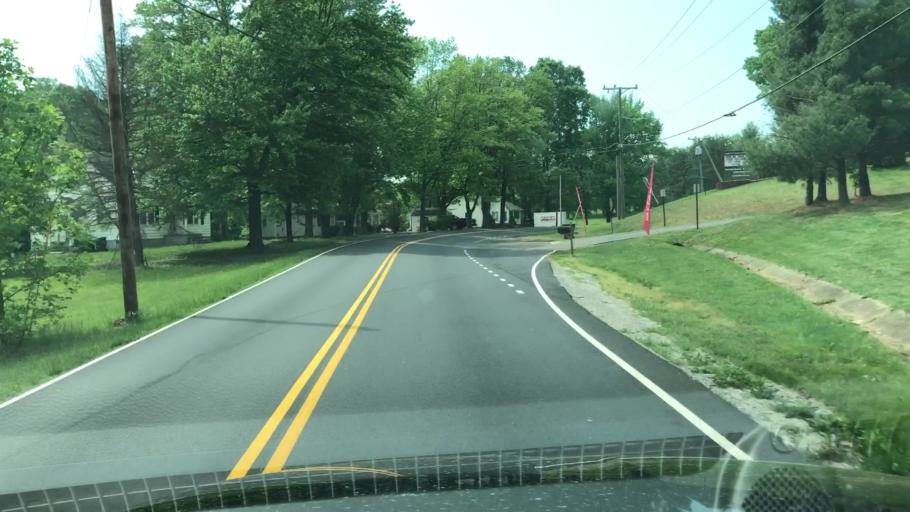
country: US
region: Virginia
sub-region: Stafford County
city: Stafford
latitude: 38.4485
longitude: -77.4883
